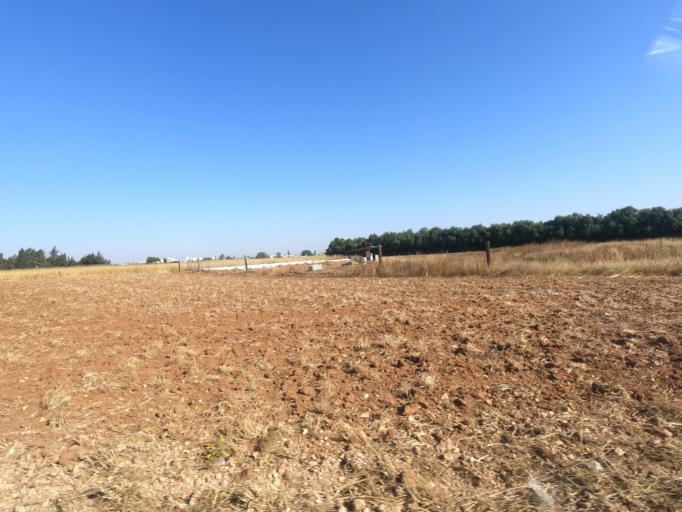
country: CY
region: Ammochostos
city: Frenaros
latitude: 35.0434
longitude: 33.9333
